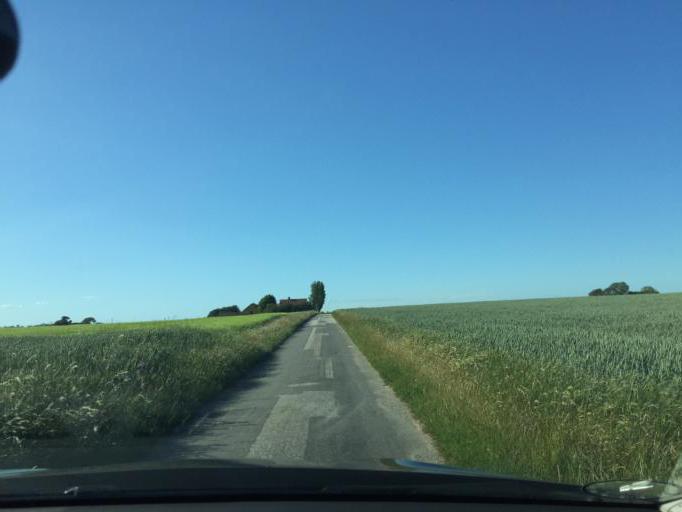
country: DK
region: Zealand
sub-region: Slagelse Kommune
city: Skaelskor
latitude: 55.2007
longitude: 11.1818
